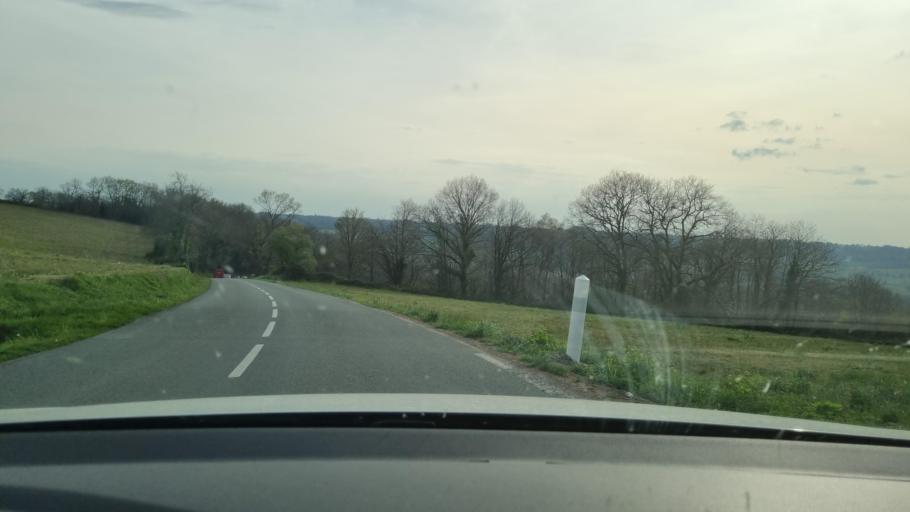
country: FR
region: Aquitaine
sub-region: Departement des Pyrenees-Atlantiques
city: Soumoulou
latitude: 43.3771
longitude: -0.1035
